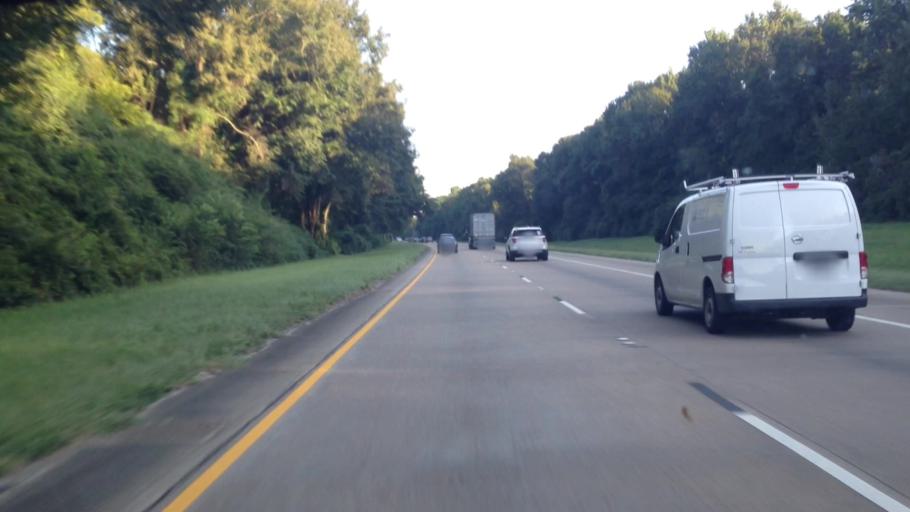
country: US
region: Louisiana
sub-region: Ascension Parish
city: Prairieville
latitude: 30.3078
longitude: -90.9943
